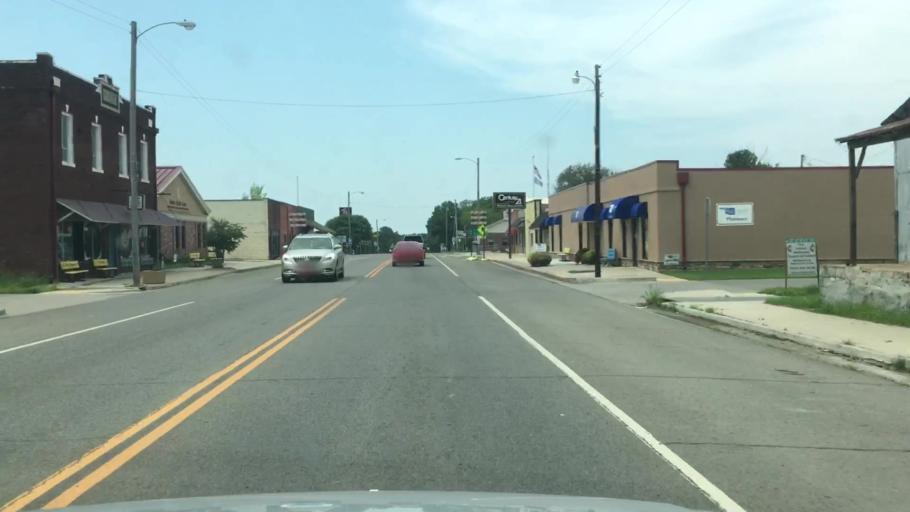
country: US
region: Oklahoma
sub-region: Muskogee County
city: Fort Gibson
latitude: 35.9328
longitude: -95.1424
